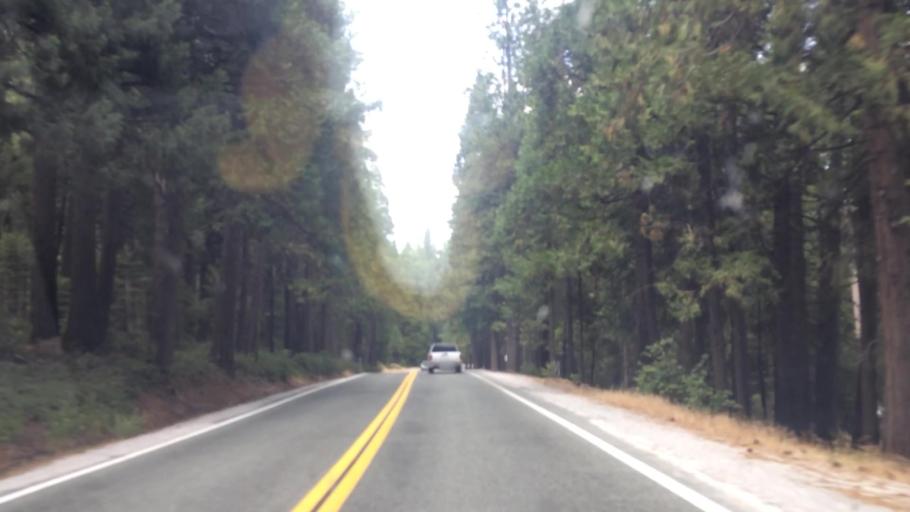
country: US
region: California
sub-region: Amador County
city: Pioneer
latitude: 38.5076
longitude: -120.4904
